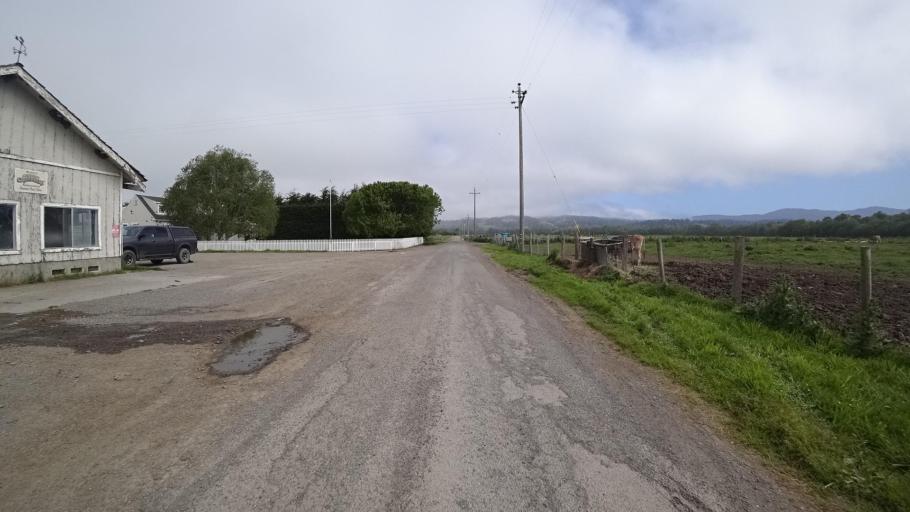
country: US
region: California
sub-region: Humboldt County
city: Fortuna
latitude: 40.5845
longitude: -124.1880
